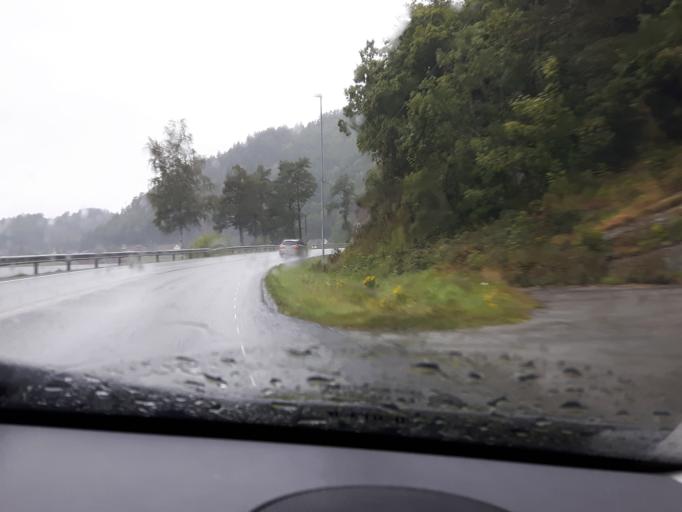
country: NO
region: Vest-Agder
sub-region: Mandal
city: Mandal
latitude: 58.0437
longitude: 7.4190
